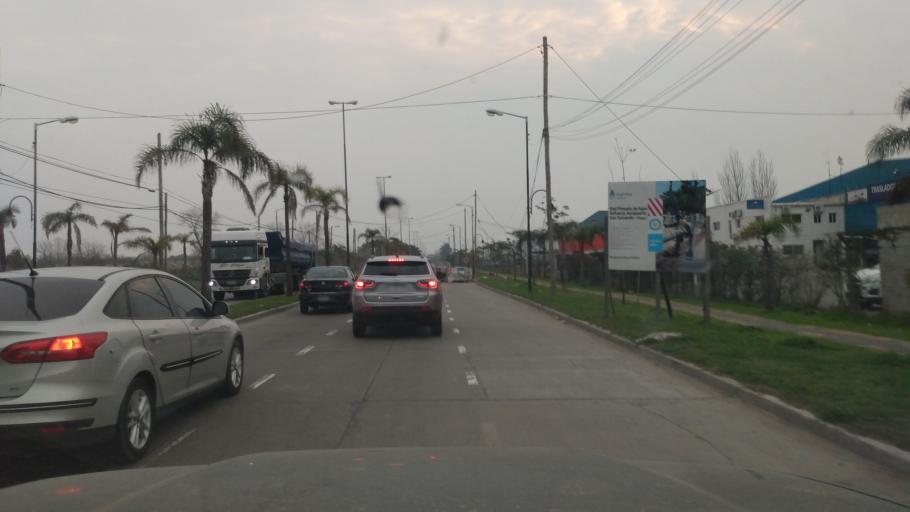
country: AR
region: Buenos Aires
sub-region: Partido de Tigre
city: Tigre
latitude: -34.4577
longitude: -58.5869
